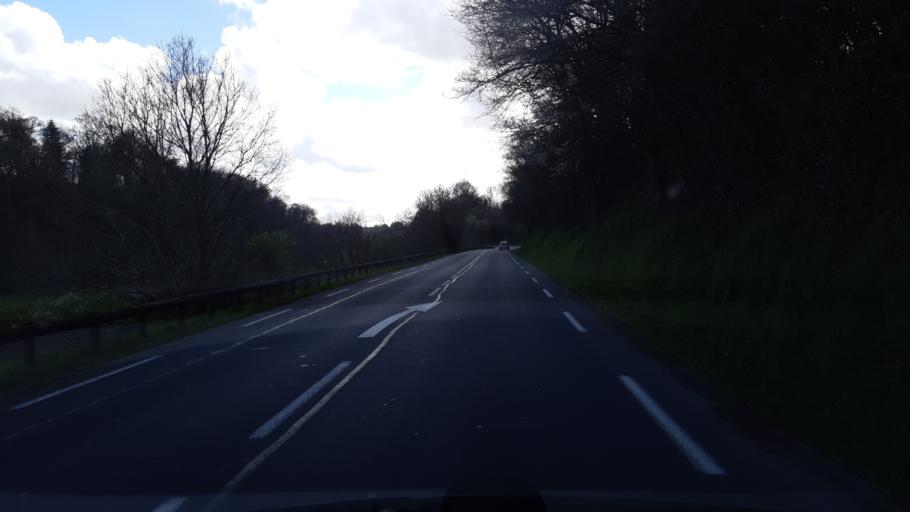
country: FR
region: Lower Normandy
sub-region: Departement de la Manche
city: Agneaux
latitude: 49.0766
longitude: -1.1253
